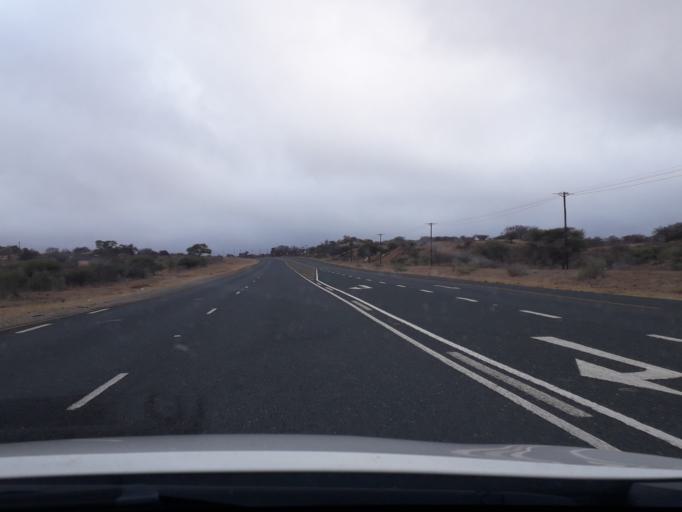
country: ZA
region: Limpopo
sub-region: Capricorn District Municipality
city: Dendron
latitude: -23.4429
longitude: 29.7437
